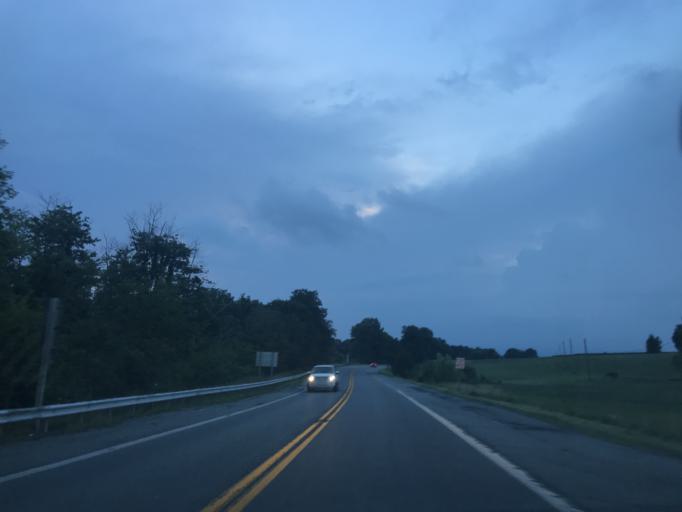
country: US
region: Maryland
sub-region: Cecil County
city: Rising Sun
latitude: 39.6964
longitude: -76.0804
